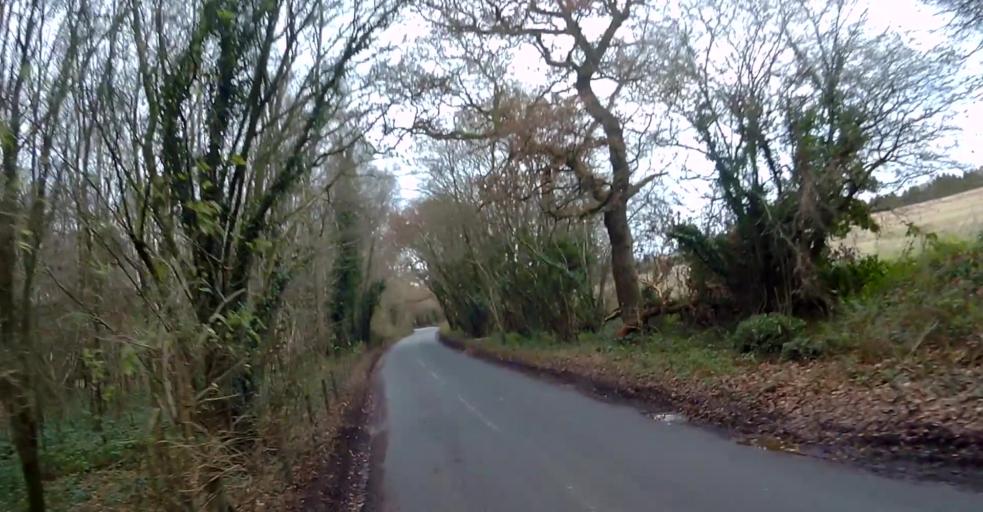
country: GB
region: England
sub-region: Hampshire
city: Basingstoke
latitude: 51.1950
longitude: -1.1634
